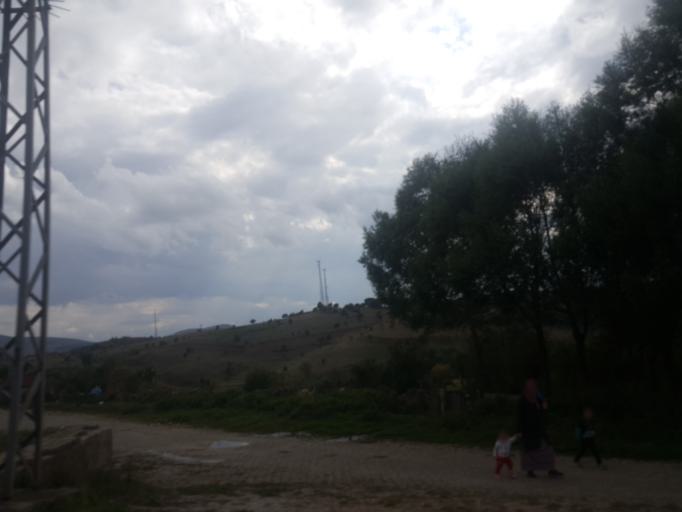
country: TR
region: Tokat
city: Bereketli
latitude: 40.5393
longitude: 37.2942
